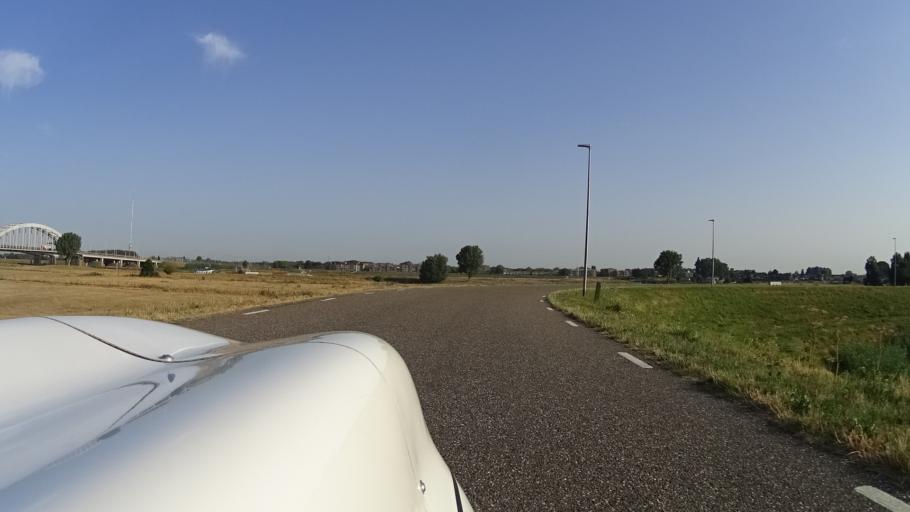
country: NL
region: Utrecht
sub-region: Gemeente Vianen
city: Vianen
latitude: 51.9953
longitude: 5.0870
